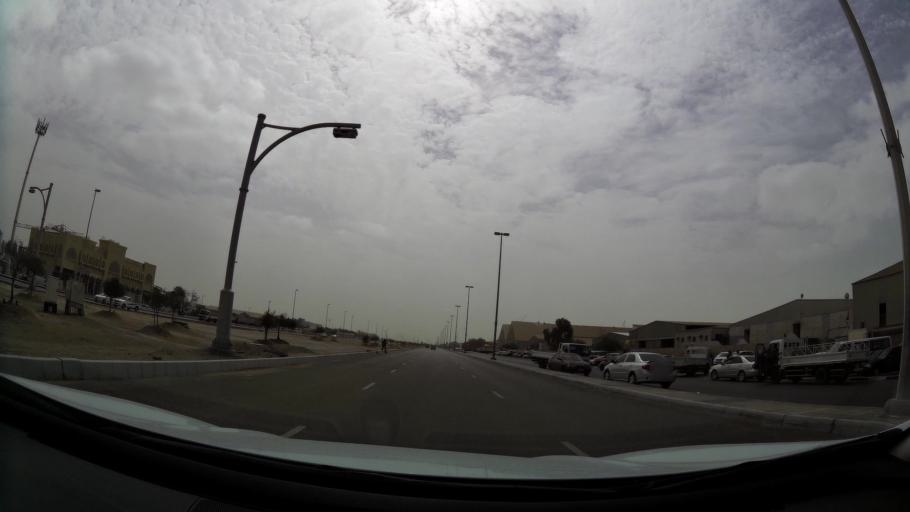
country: AE
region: Abu Dhabi
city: Abu Dhabi
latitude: 24.3762
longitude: 54.4712
